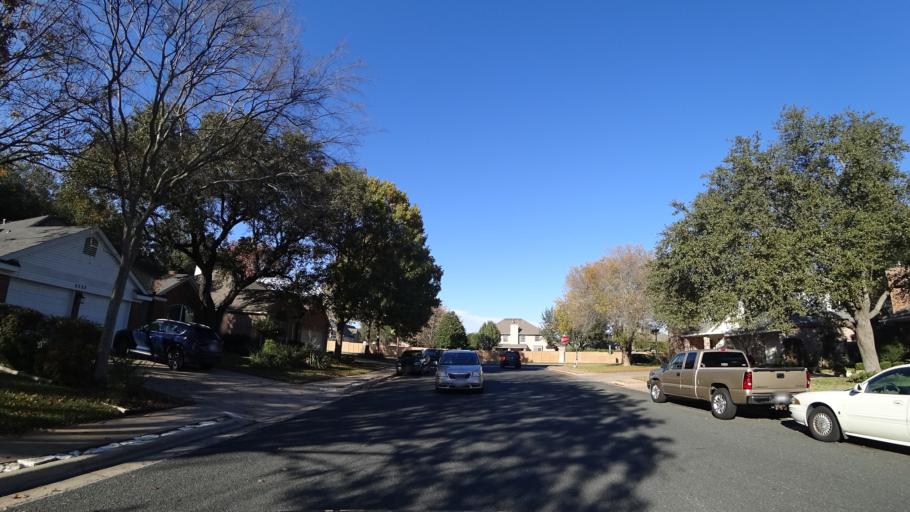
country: US
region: Texas
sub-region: Williamson County
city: Brushy Creek
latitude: 30.4946
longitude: -97.7424
